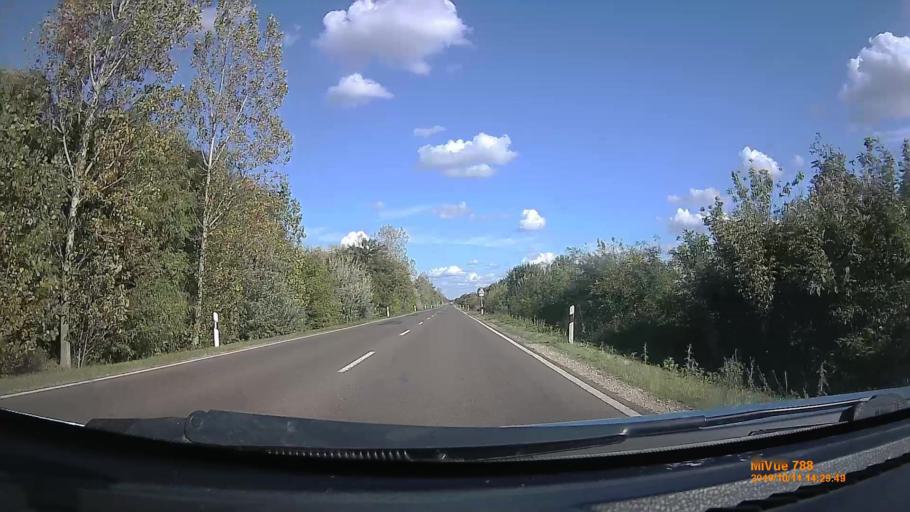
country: HU
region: Hajdu-Bihar
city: Balmazujvaros
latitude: 47.5594
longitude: 21.3892
